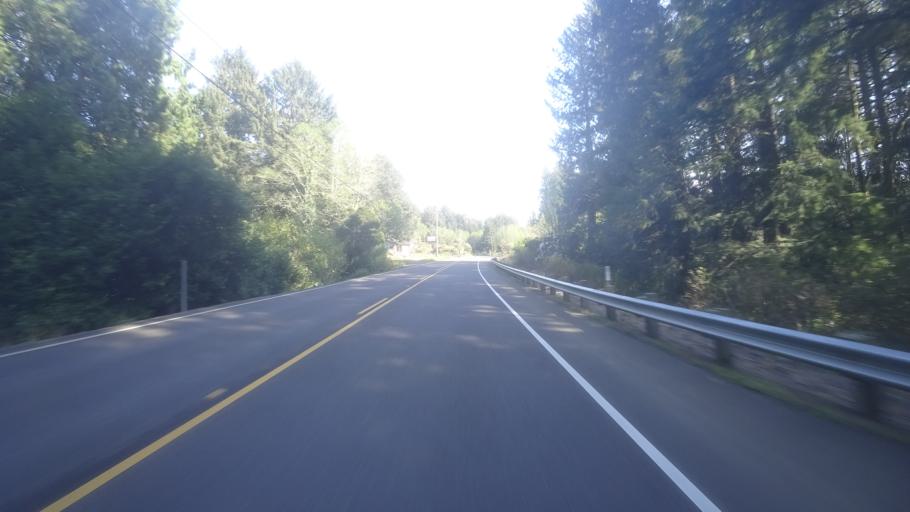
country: US
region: Oregon
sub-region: Lane County
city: Florence
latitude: 44.0919
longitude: -124.1108
